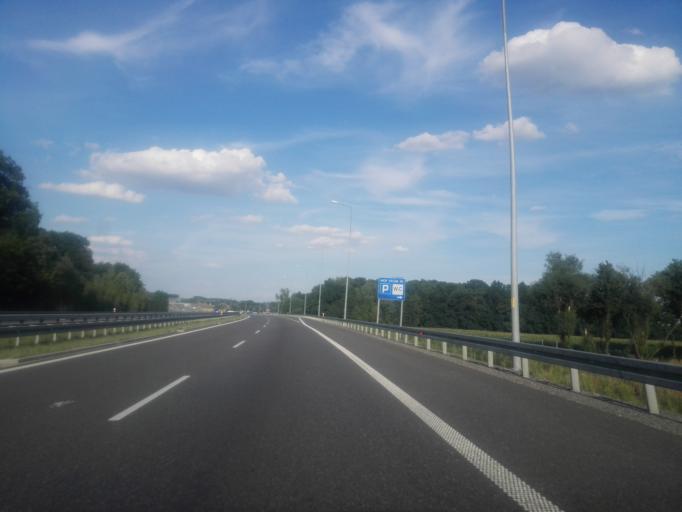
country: PL
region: Lower Silesian Voivodeship
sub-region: Powiat olesnicki
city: Sycow
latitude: 51.2937
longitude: 17.7261
